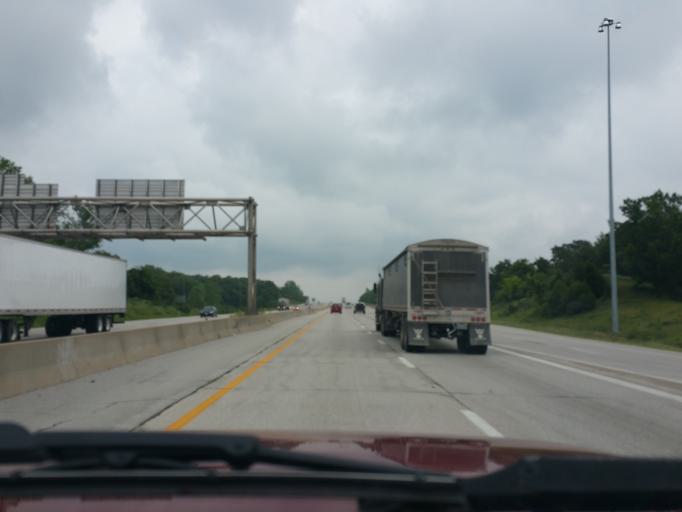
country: US
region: Kansas
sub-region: Wyandotte County
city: Edwardsville
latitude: 39.1058
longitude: -94.8012
